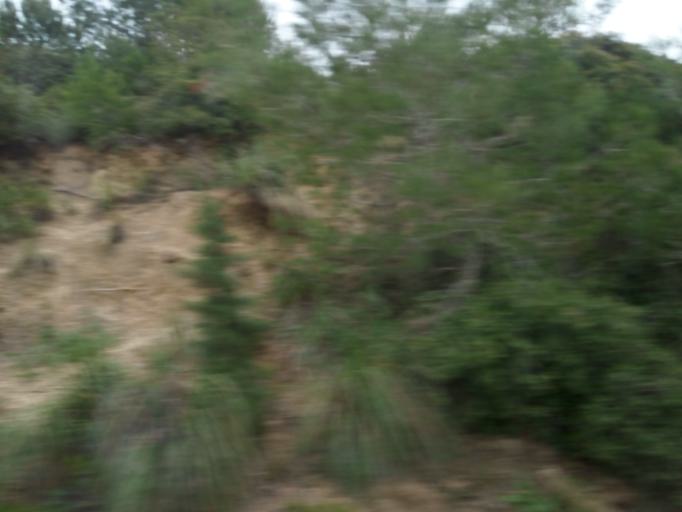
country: DZ
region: Tipaza
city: Tipasa
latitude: 36.5822
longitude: 2.5422
